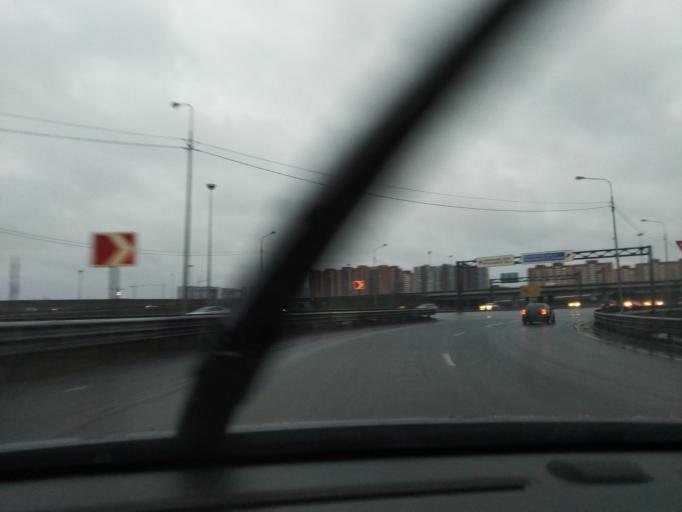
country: RU
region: St.-Petersburg
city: Sosnovaya Polyana
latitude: 59.8017
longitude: 30.1581
